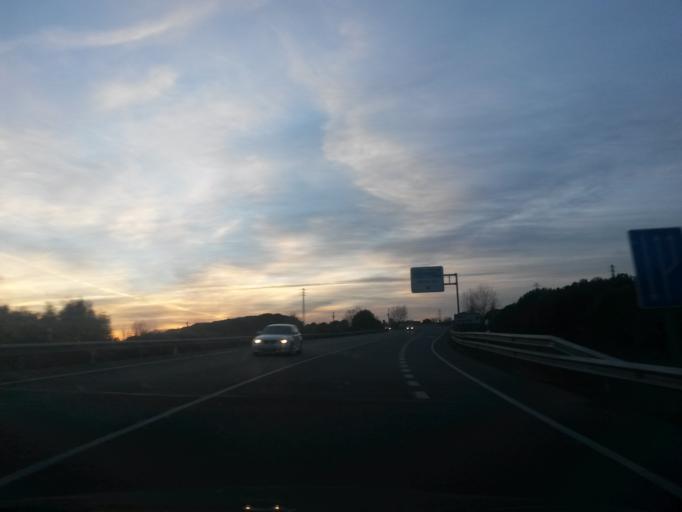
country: ES
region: Catalonia
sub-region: Provincia de Girona
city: Fornells de la Selva
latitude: 41.9420
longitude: 2.8225
